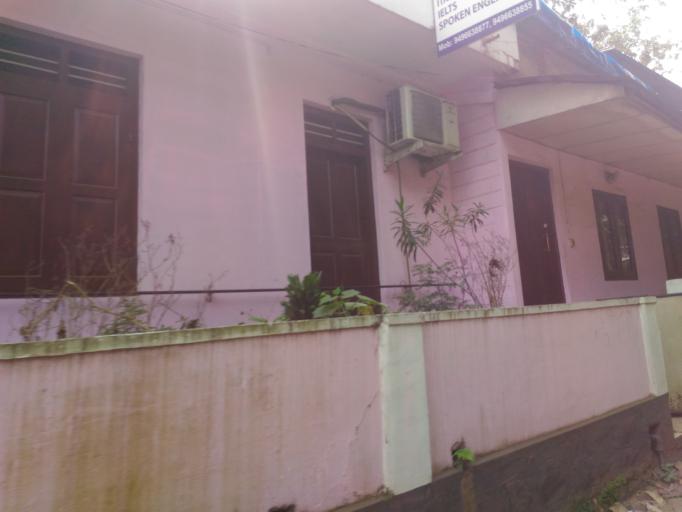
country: IN
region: Kerala
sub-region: Kottayam
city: Lalam
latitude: 9.7094
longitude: 76.6729
